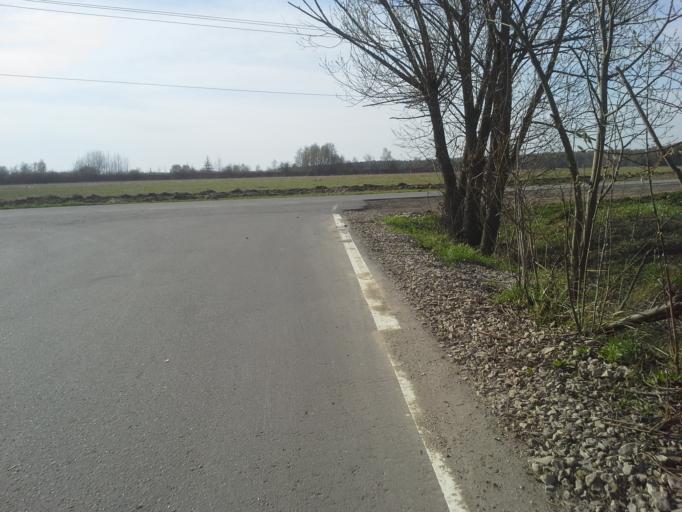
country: RU
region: Moskovskaya
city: Vatutinki
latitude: 55.4623
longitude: 37.3771
